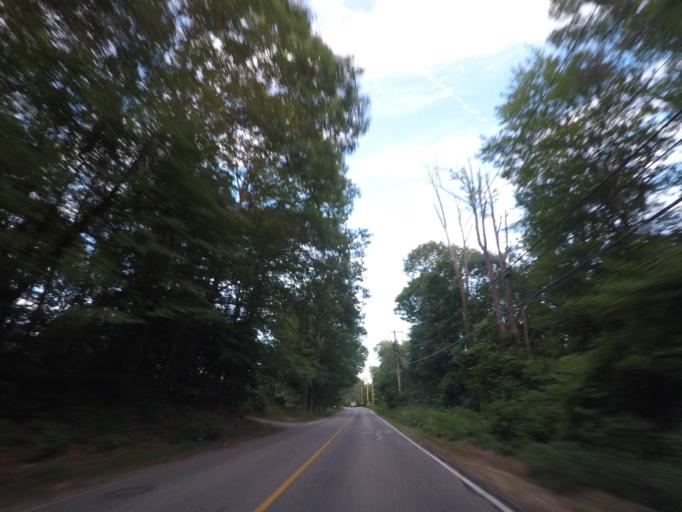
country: US
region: Massachusetts
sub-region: Worcester County
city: Warren
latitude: 42.1924
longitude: -72.1803
